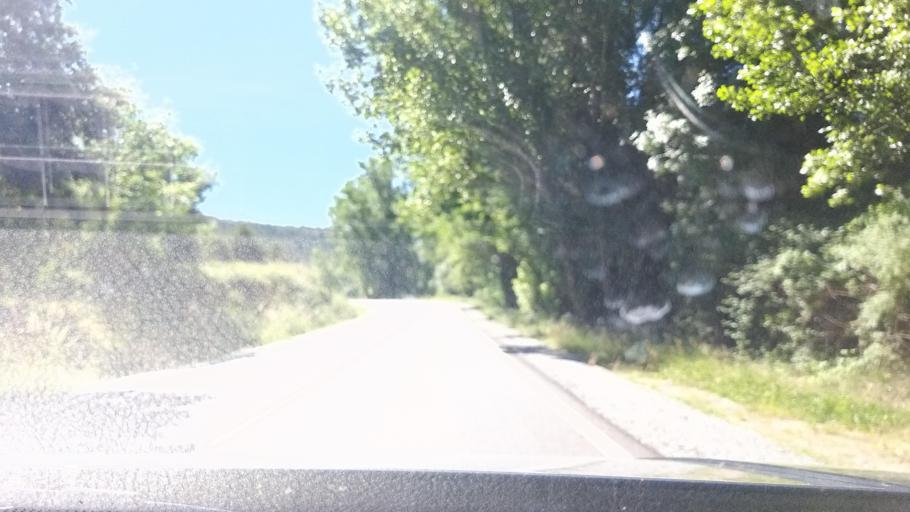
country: ES
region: Castille and Leon
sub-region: Provincia de Segovia
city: Pedraza
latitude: 41.1398
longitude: -3.8206
